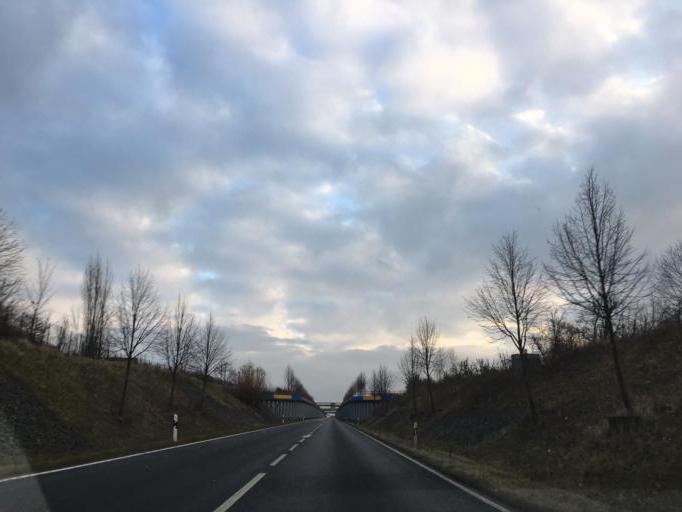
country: DE
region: Saxony
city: Grossposna
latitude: 51.2856
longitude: 12.4500
